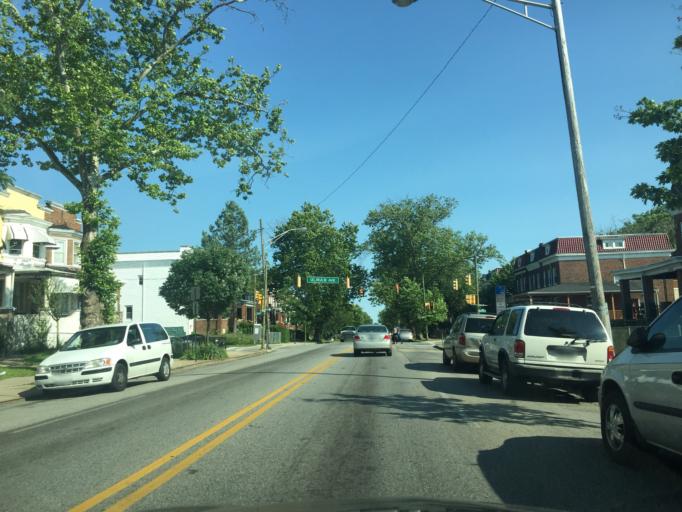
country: US
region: Maryland
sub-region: City of Baltimore
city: Baltimore
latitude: 39.3293
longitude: -76.6606
